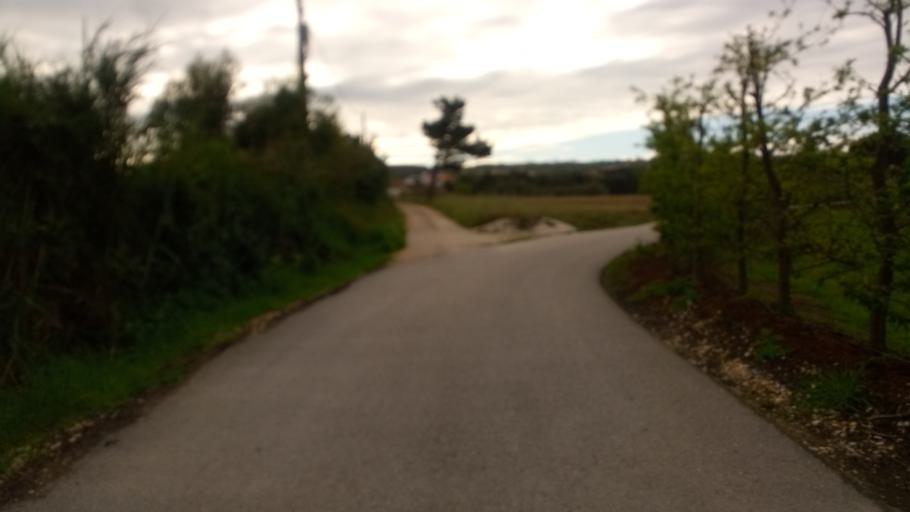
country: PT
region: Leiria
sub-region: Caldas da Rainha
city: Caldas da Rainha
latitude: 39.4530
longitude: -9.1726
